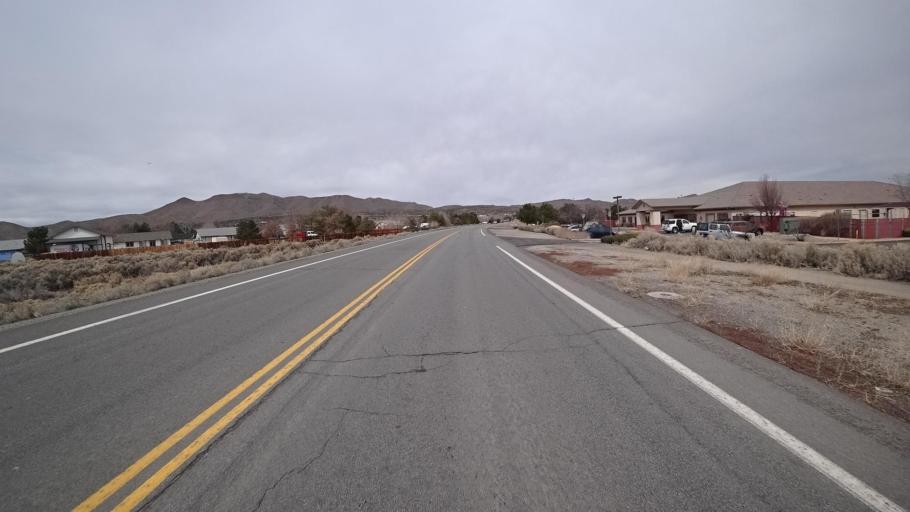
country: US
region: Nevada
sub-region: Washoe County
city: Spanish Springs
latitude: 39.6421
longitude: -119.7202
